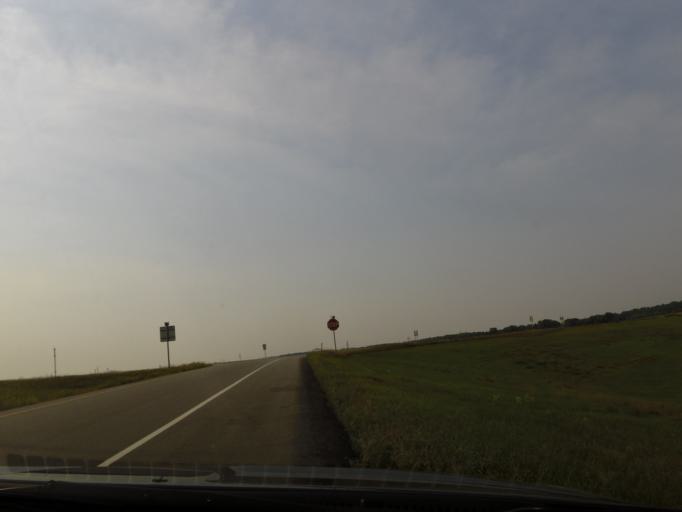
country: US
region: North Dakota
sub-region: Cass County
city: Horace
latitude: 46.6308
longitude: -96.8332
